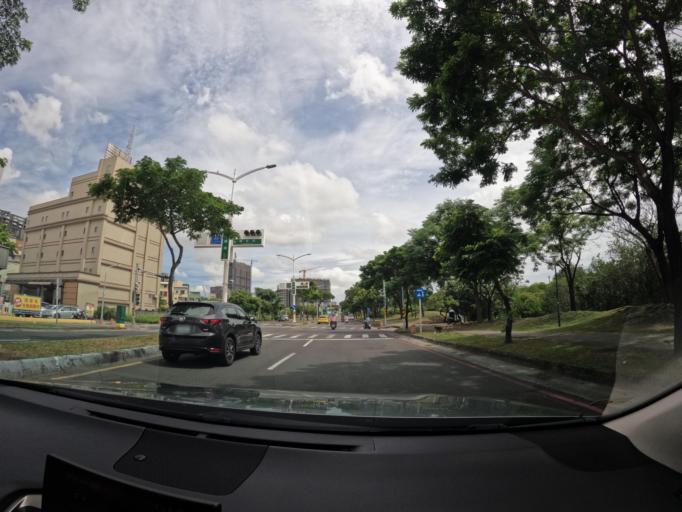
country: TW
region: Kaohsiung
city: Kaohsiung
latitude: 22.6484
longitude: 120.2880
